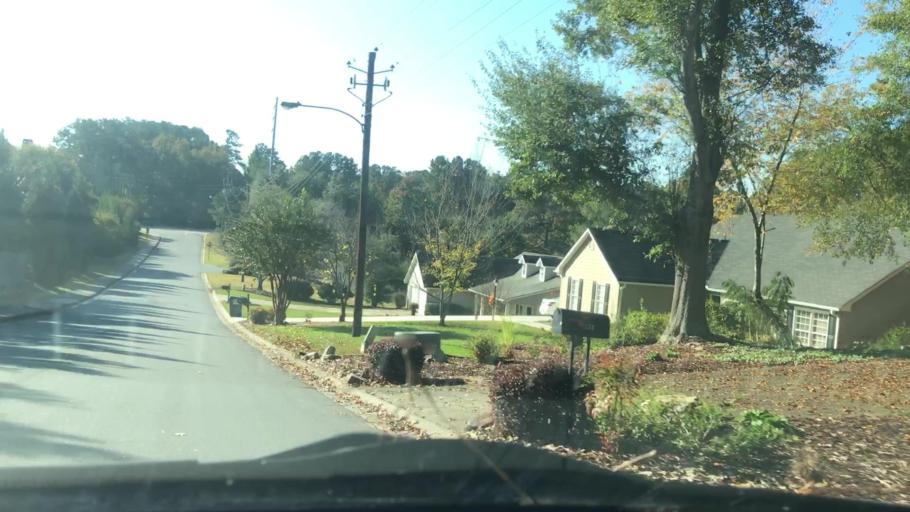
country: US
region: Georgia
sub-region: Fulton County
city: Roswell
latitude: 34.0031
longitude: -84.4031
